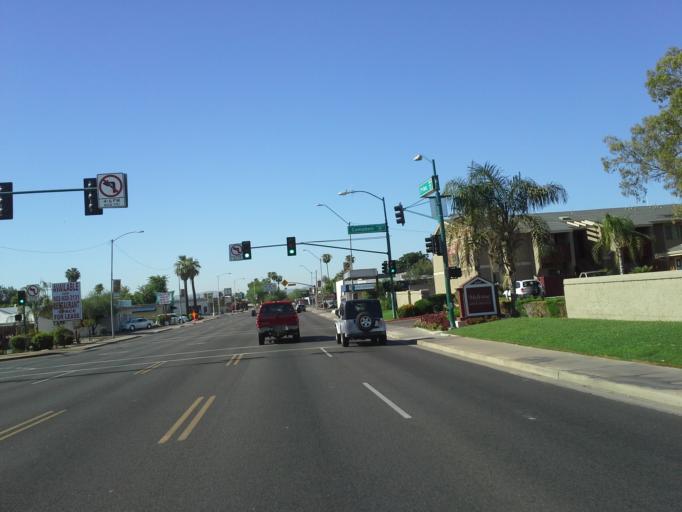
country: US
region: Arizona
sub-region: Maricopa County
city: Phoenix
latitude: 33.5025
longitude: -112.0825
